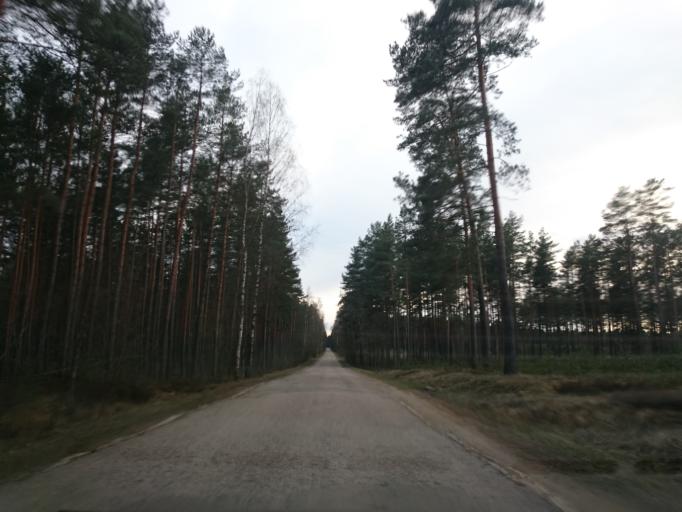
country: LV
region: Riga
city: Bergi
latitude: 57.0068
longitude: 24.3191
